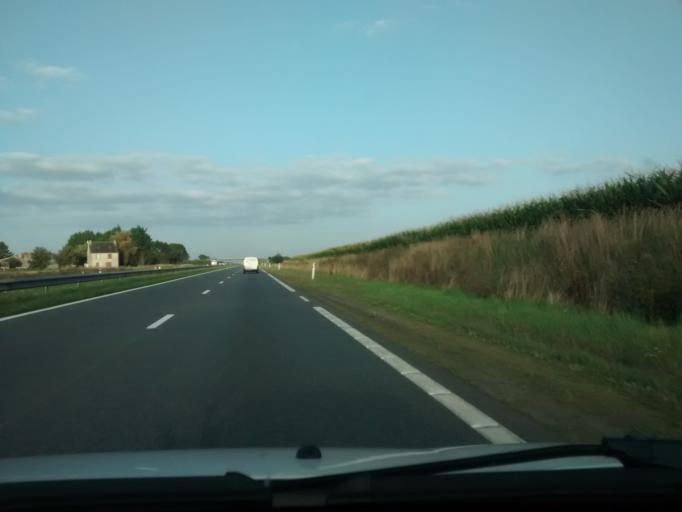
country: FR
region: Brittany
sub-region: Departement des Cotes-d'Armor
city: Pordic
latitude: 48.5451
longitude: -2.8149
